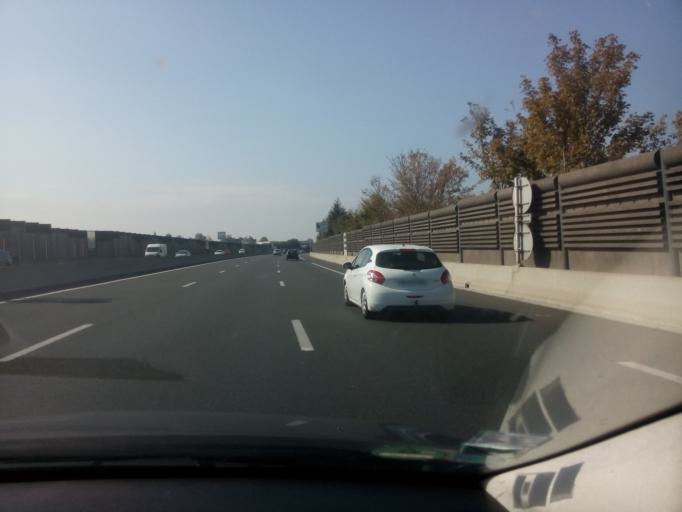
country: FR
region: Pays de la Loire
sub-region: Departement de Maine-et-Loire
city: Ecouflant
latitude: 47.4945
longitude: -0.5252
